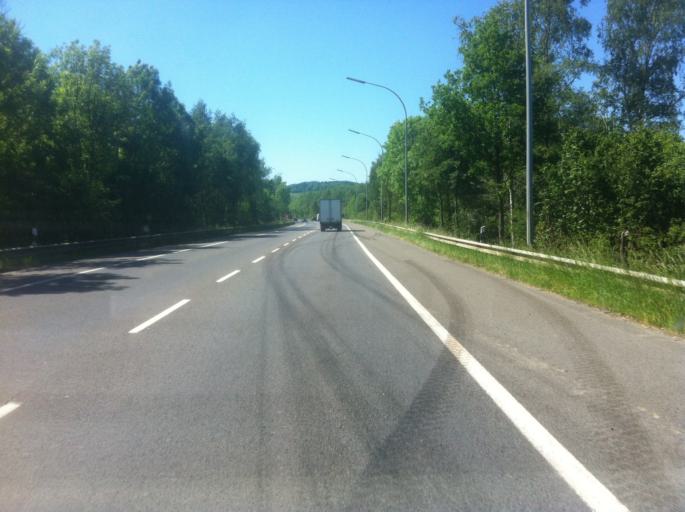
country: LU
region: Luxembourg
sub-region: Canton de Capellen
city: Garnich
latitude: 49.6407
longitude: 5.9557
